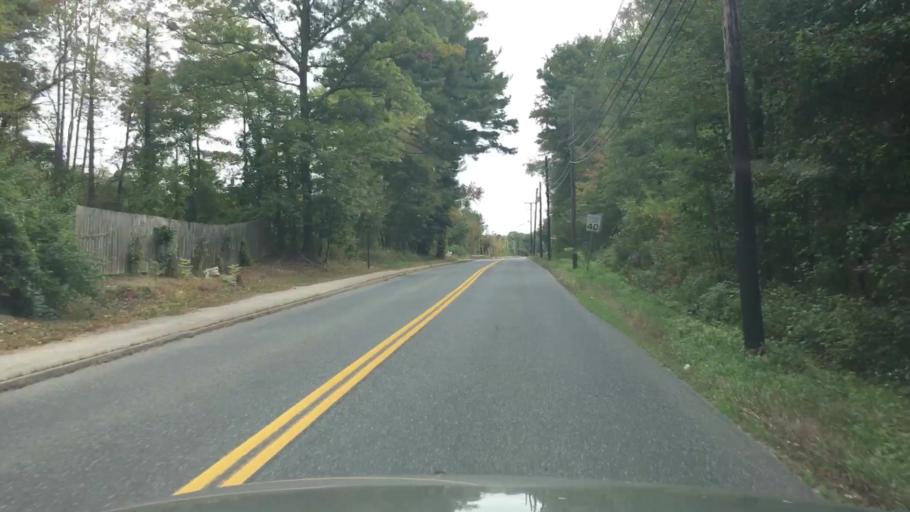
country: US
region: Massachusetts
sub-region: Worcester County
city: Charlton
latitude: 42.1432
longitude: -71.9826
